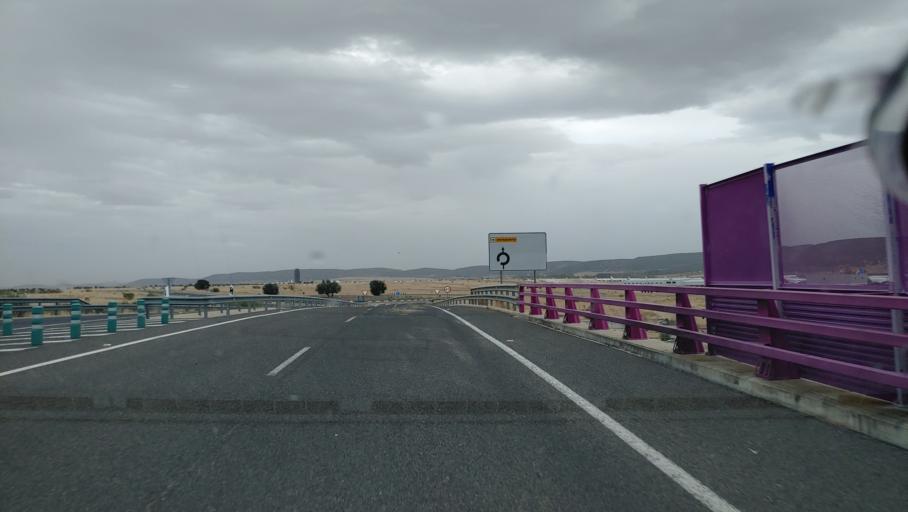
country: ES
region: Castille-La Mancha
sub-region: Provincia de Ciudad Real
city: Canada de Calatrava
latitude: 38.8725
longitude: -3.9915
